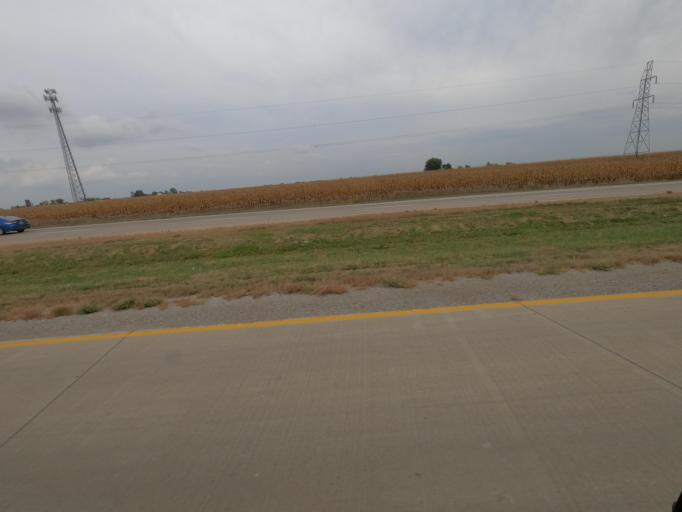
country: US
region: Iowa
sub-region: Jasper County
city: Monroe
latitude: 41.5071
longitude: -93.0838
